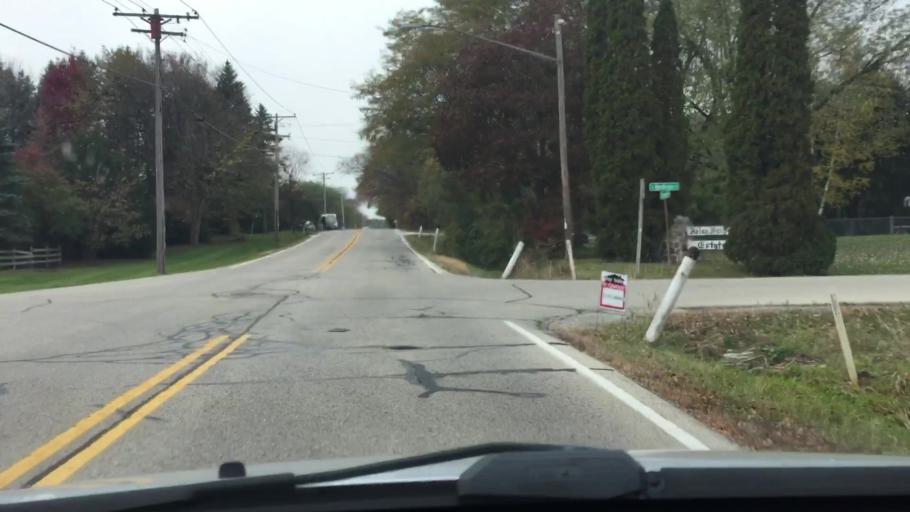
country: US
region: Wisconsin
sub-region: Milwaukee County
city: Hales Corners
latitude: 42.9445
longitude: -88.0800
